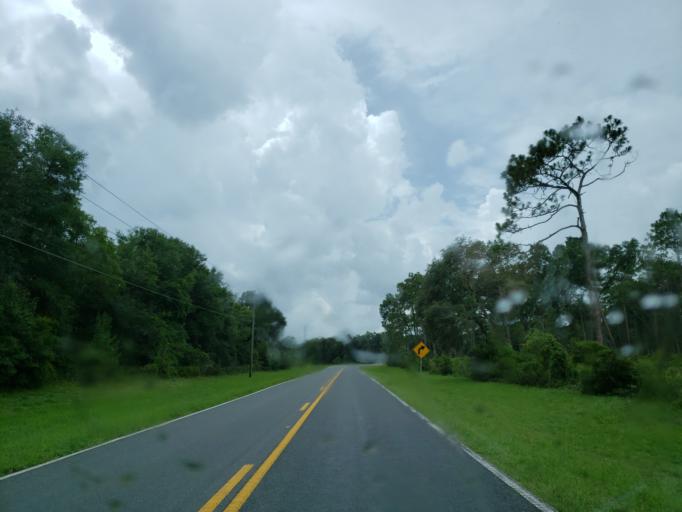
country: US
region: Florida
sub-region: Citrus County
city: Floral City
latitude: 28.6465
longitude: -82.2897
